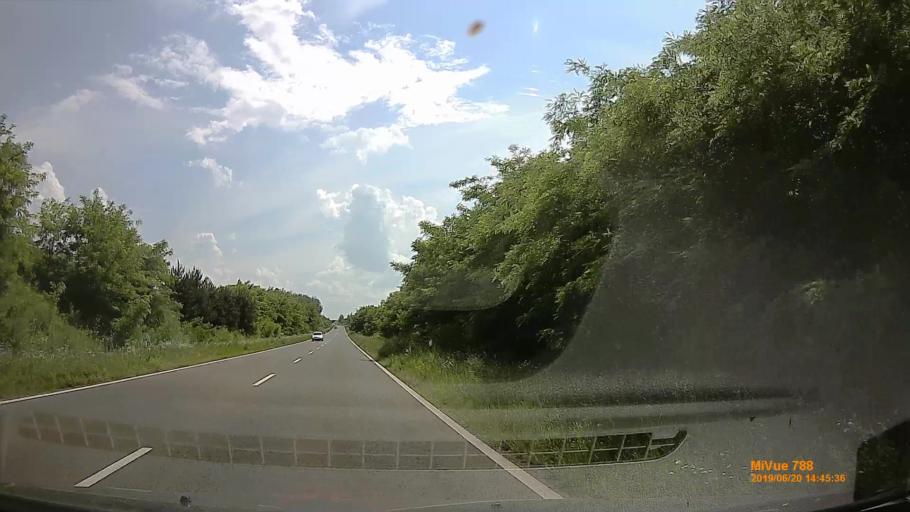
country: HU
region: Baranya
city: Kozarmisleny
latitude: 46.0486
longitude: 18.2737
